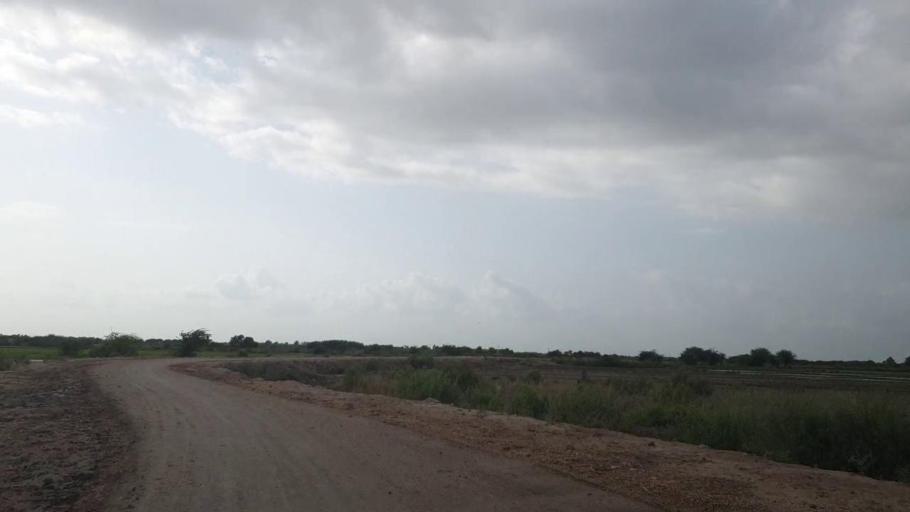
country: PK
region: Sindh
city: Kadhan
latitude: 24.5816
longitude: 69.0578
